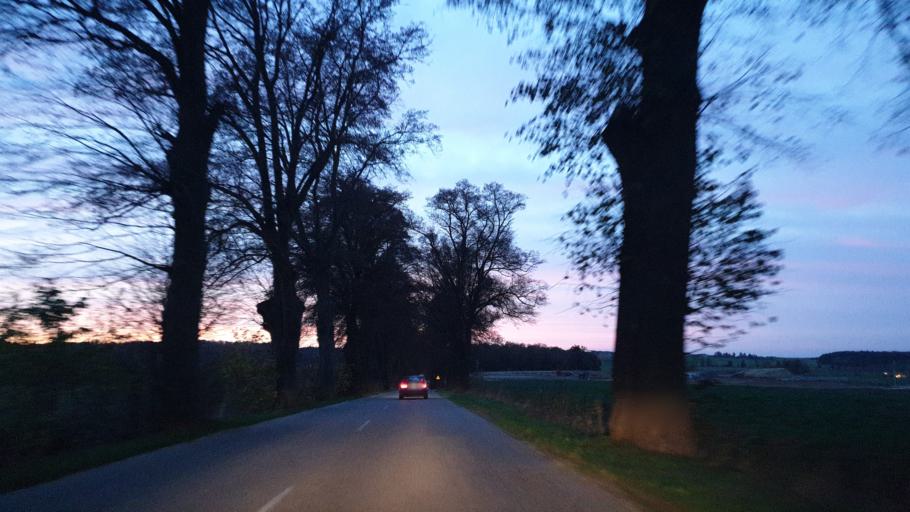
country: PL
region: Pomeranian Voivodeship
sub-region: Powiat pucki
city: Krokowa
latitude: 54.7623
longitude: 18.2408
